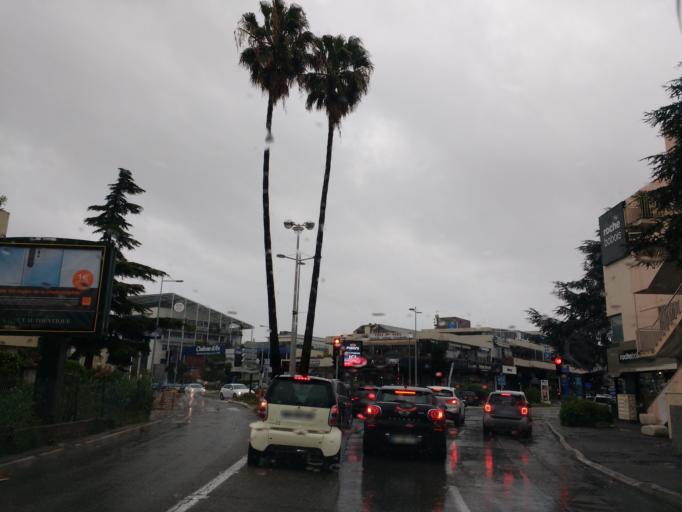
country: FR
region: Provence-Alpes-Cote d'Azur
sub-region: Departement des Alpes-Maritimes
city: Saint-Laurent-du-Var
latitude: 43.6602
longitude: 7.1929
